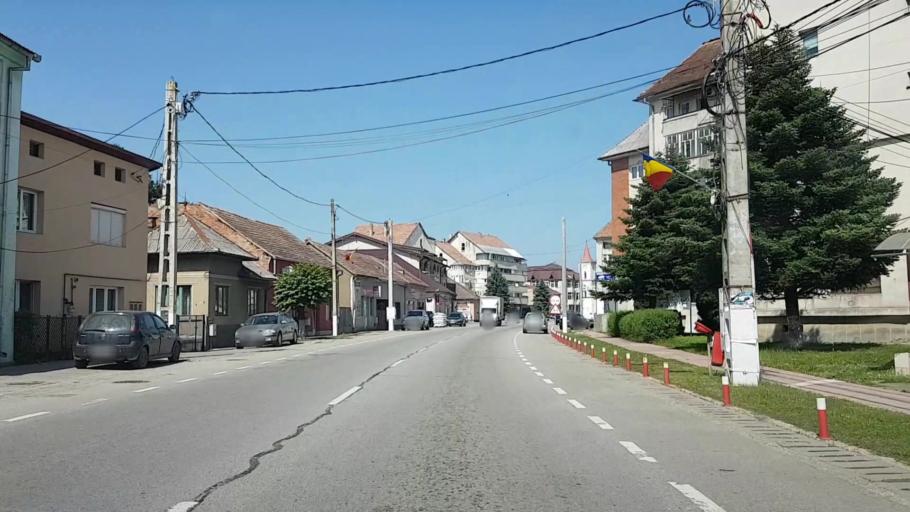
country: RO
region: Bistrita-Nasaud
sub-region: Comuna Beclean
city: Beclean
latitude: 47.1779
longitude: 24.1735
